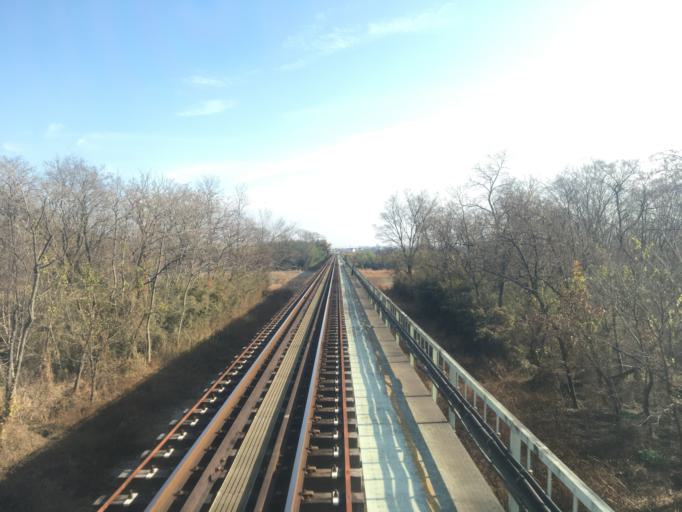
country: JP
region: Gunma
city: Fujioka
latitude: 36.2256
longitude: 139.0867
